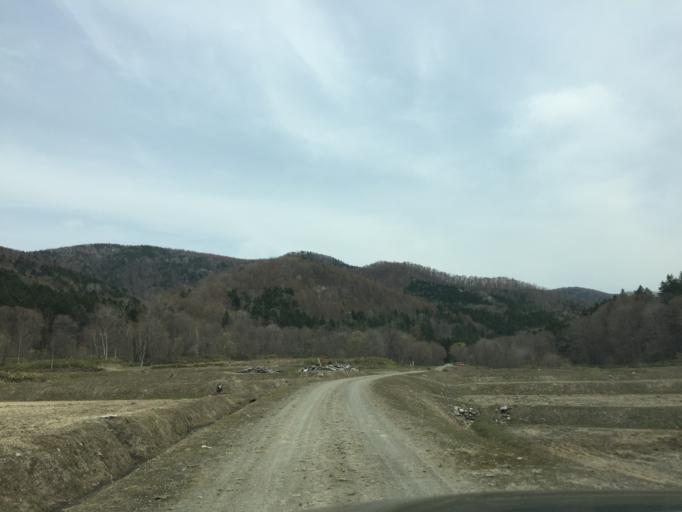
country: JP
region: Hokkaido
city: Ashibetsu
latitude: 43.6225
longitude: 142.2248
